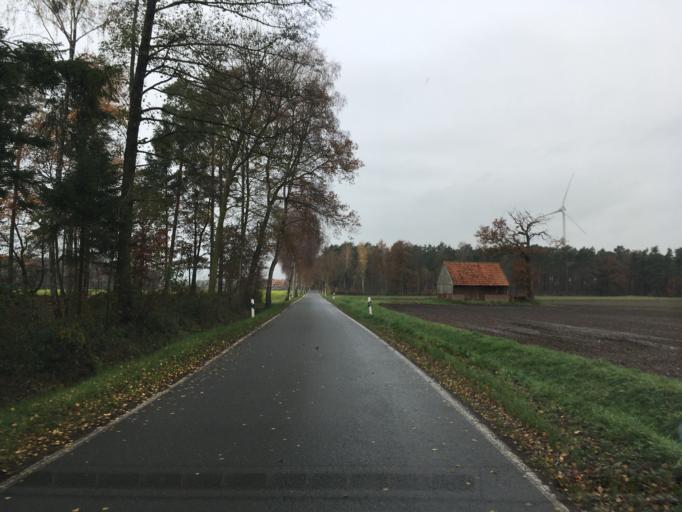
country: DE
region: North Rhine-Westphalia
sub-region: Regierungsbezirk Munster
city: Ahaus
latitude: 52.0194
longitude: 6.9964
